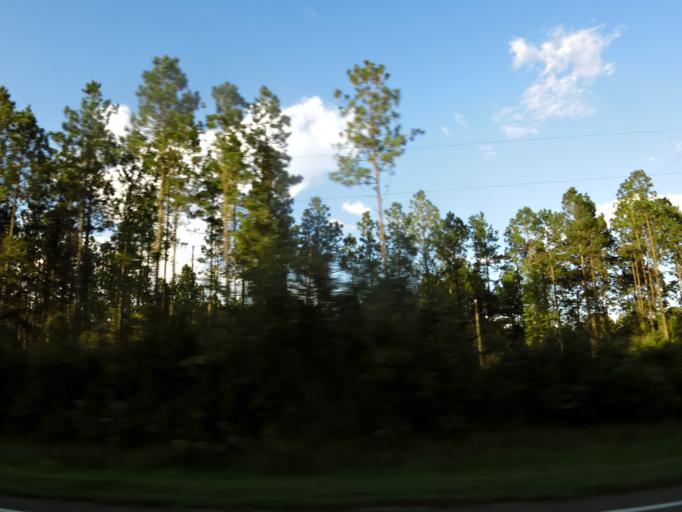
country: US
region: Georgia
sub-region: Lowndes County
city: Valdosta
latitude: 30.7918
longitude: -83.1805
